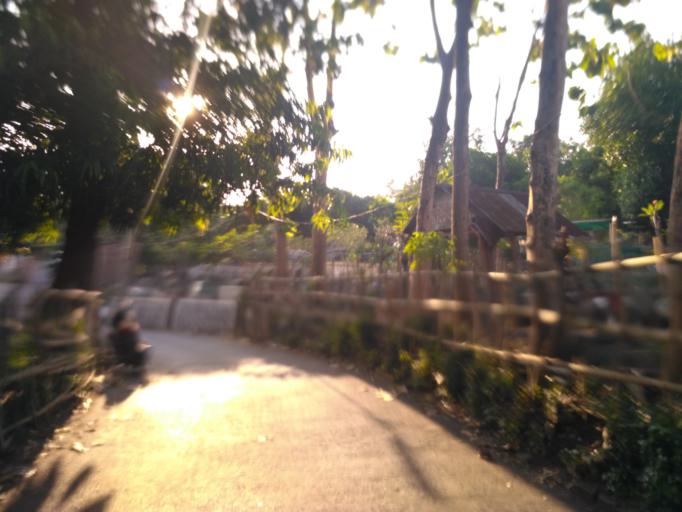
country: ID
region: Central Java
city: Semarang
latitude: -6.9912
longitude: 110.4132
